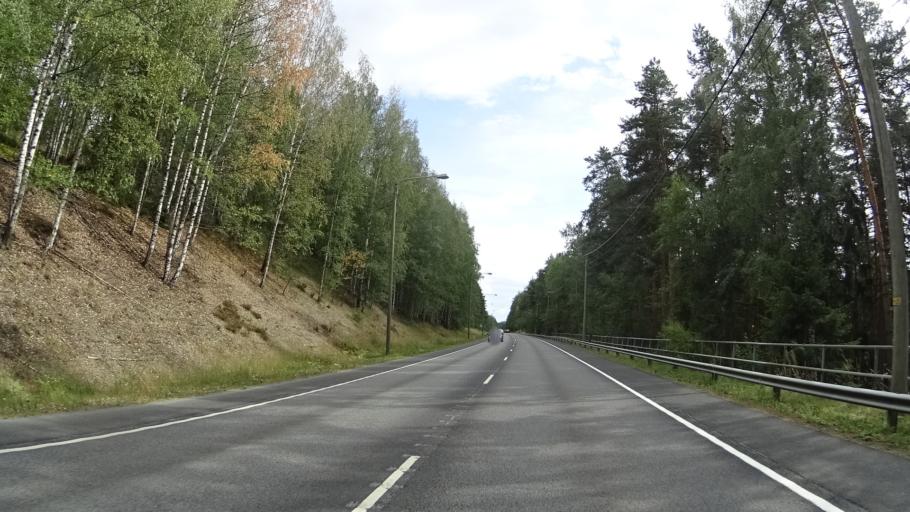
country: FI
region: Pirkanmaa
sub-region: Tampere
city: Kangasala
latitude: 61.4305
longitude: 24.1294
